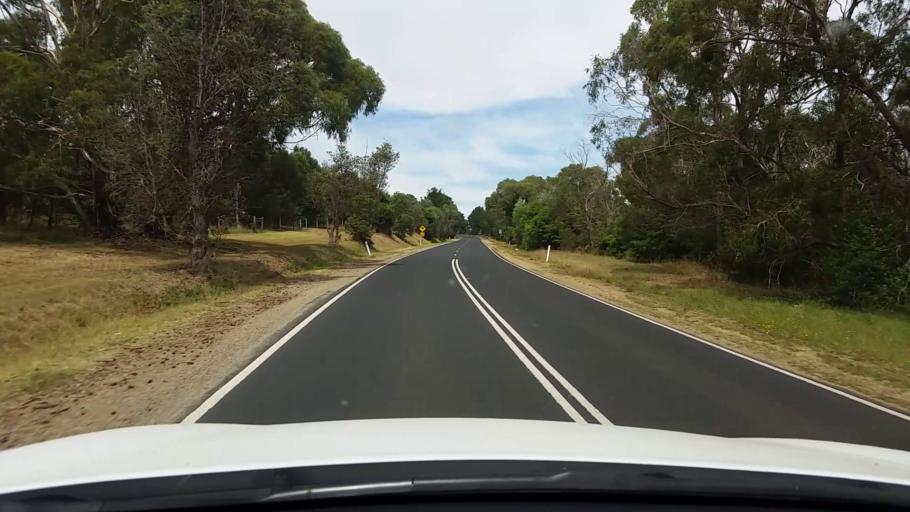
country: AU
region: Victoria
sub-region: Mornington Peninsula
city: Merricks
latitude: -38.4353
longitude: 145.0411
